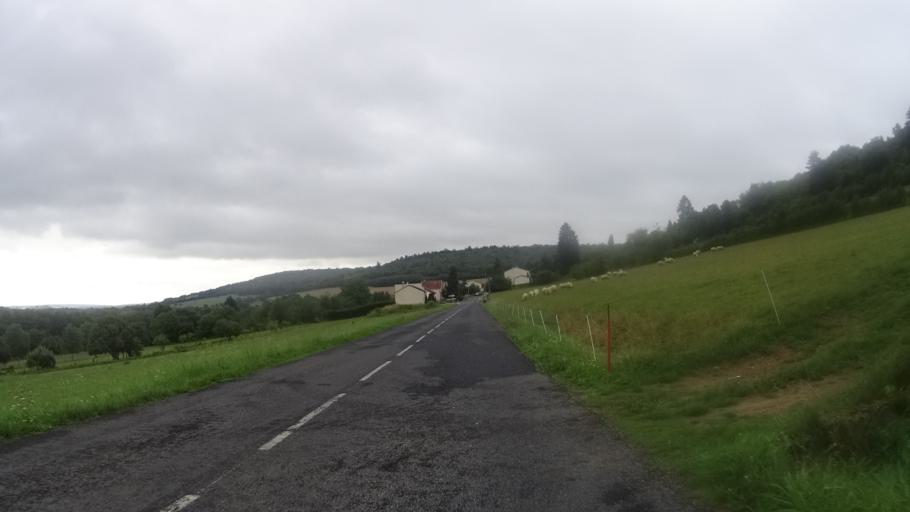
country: FR
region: Lorraine
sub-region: Departement de Meurthe-et-Moselle
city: Chaligny
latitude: 48.6272
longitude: 6.0439
